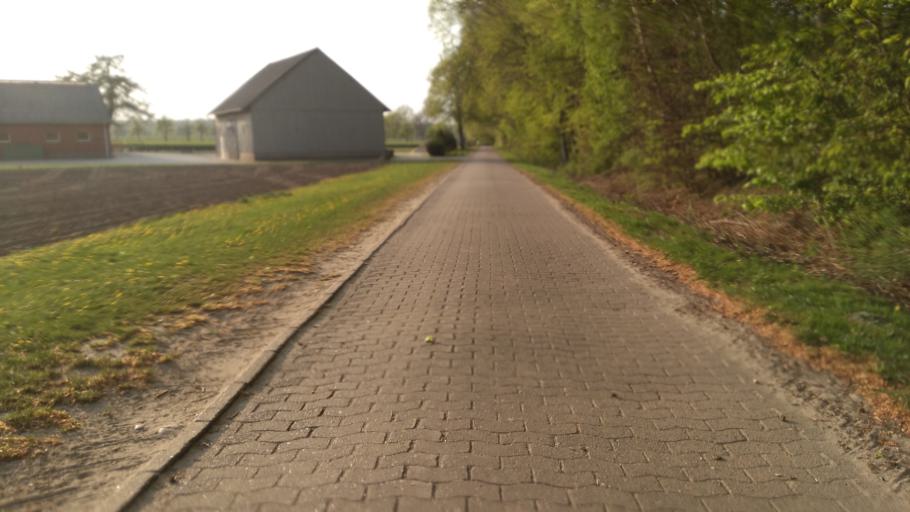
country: DE
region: Lower Saxony
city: Nottensdorf
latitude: 53.4681
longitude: 9.6359
